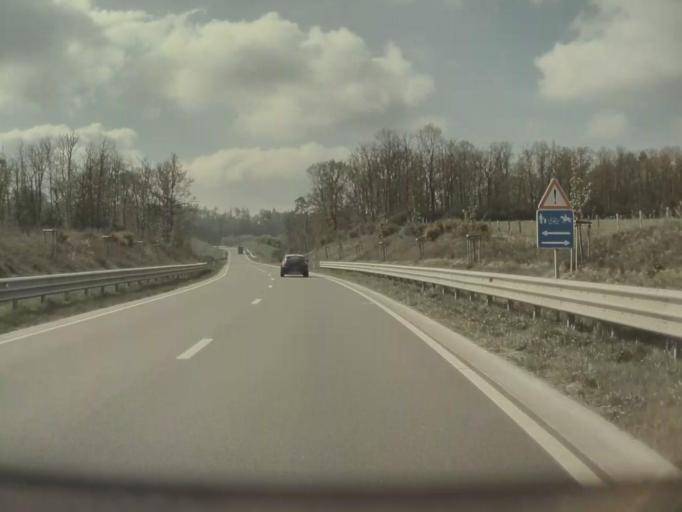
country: BE
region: Wallonia
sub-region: Province du Luxembourg
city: Marche-en-Famenne
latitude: 50.2221
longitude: 5.3145
